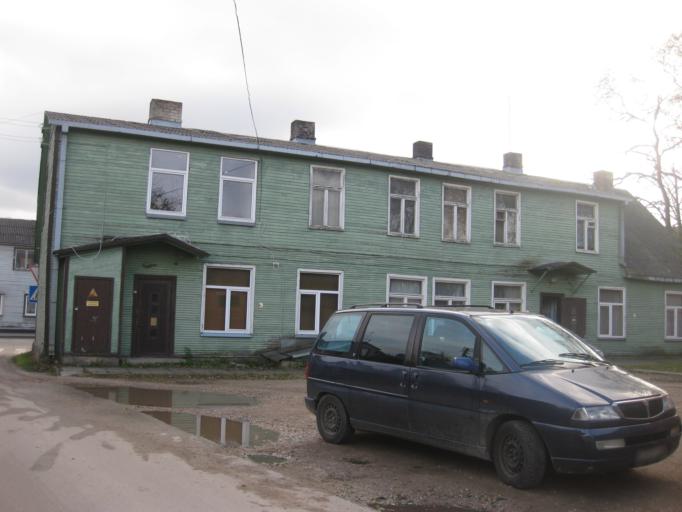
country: LT
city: Prienai
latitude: 54.6391
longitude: 23.9469
